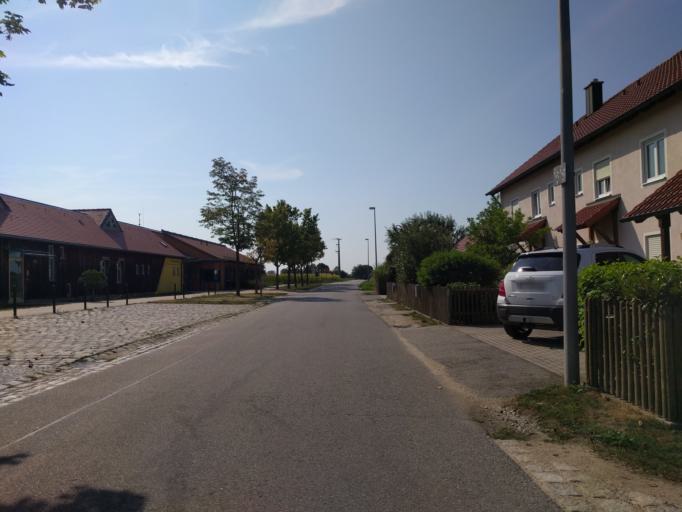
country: DE
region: Bavaria
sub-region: Upper Palatinate
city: Donaustauf
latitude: 49.0137
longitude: 12.2344
